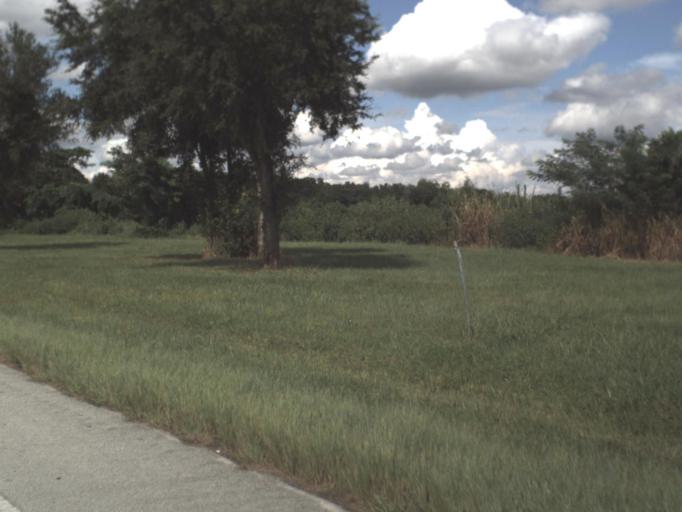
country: US
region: Florida
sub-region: Manatee County
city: Ellenton
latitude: 27.5926
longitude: -82.4255
